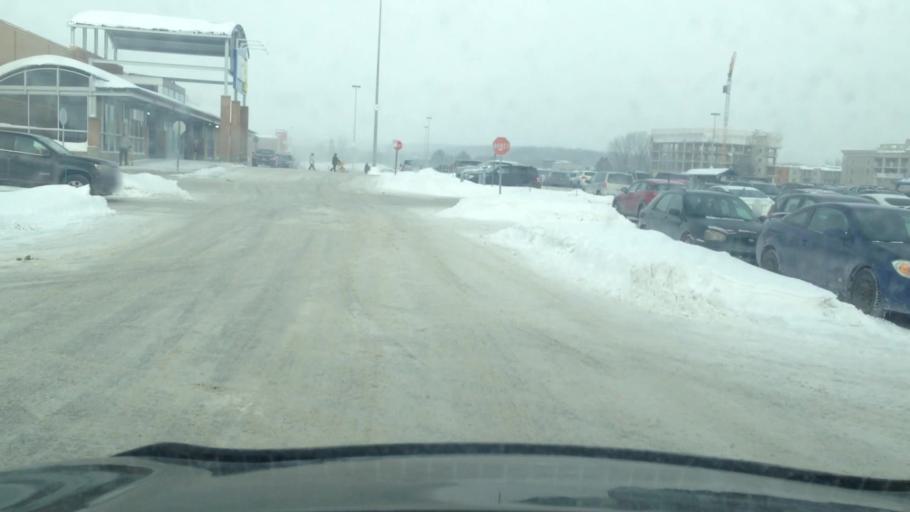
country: CA
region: Quebec
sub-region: Laurentides
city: Saint-Jerome
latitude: 45.7923
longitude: -74.0167
